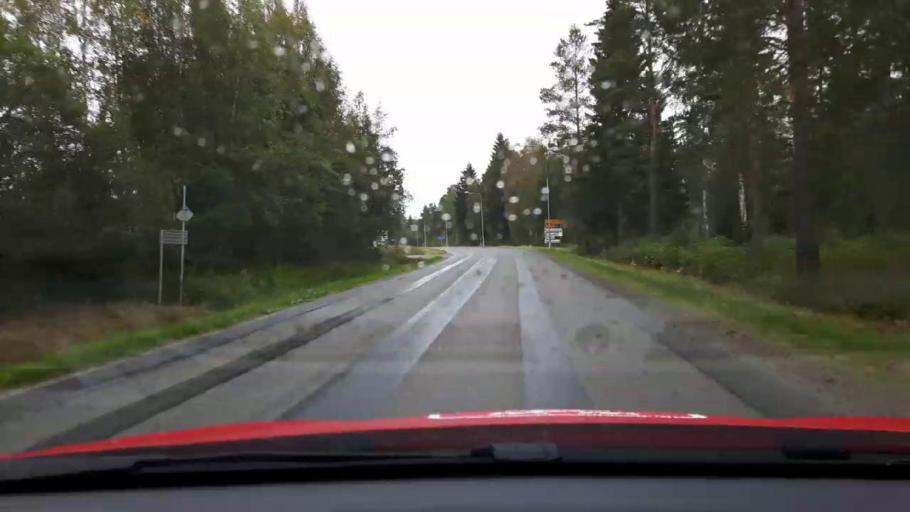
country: SE
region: Jaemtland
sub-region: Bergs Kommun
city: Hoverberg
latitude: 62.7723
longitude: 14.4298
